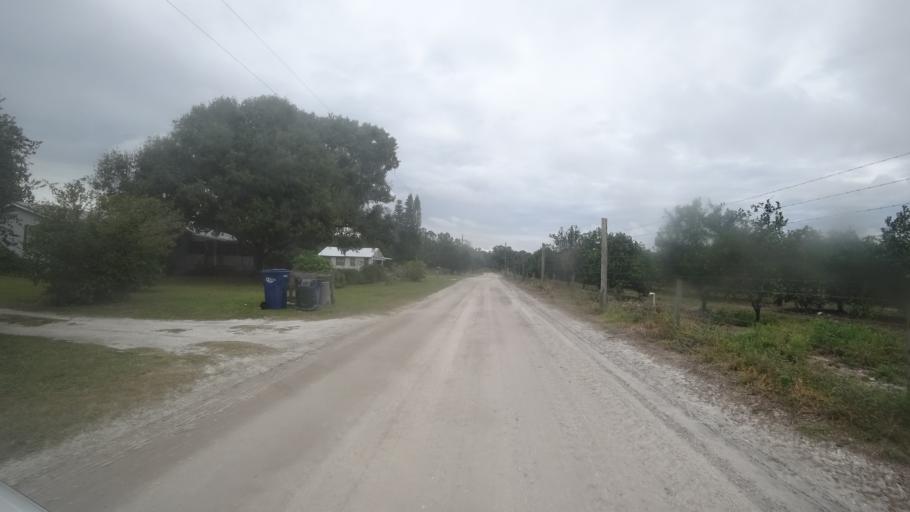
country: US
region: Florida
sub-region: Hillsborough County
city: Wimauma
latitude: 27.5712
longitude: -82.1376
